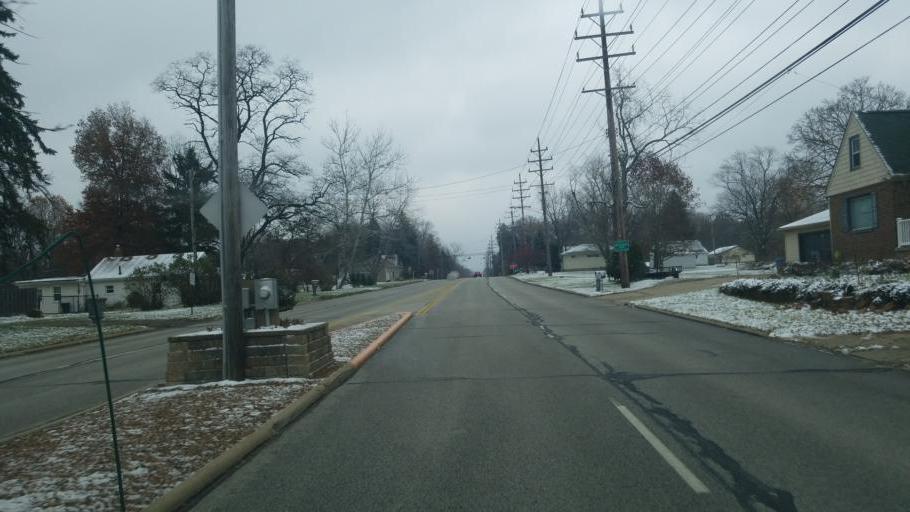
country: US
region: Ohio
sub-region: Cuyahoga County
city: Oakwood
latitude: 41.3579
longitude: -81.5103
